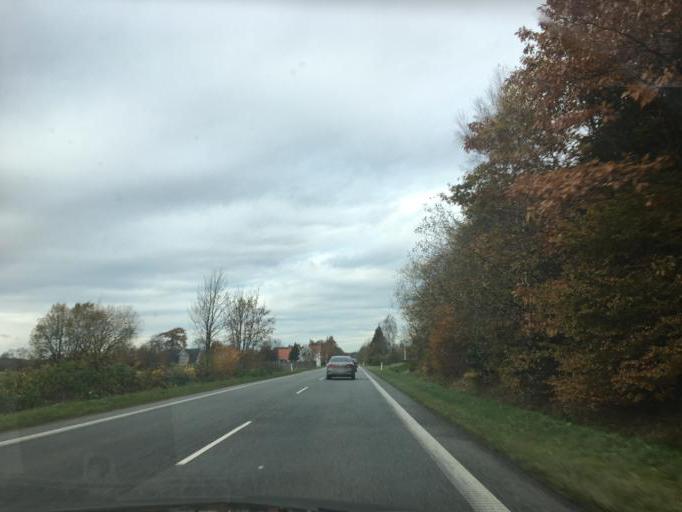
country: DK
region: South Denmark
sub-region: Vejle Kommune
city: Vejle
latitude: 55.6247
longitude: 9.4938
